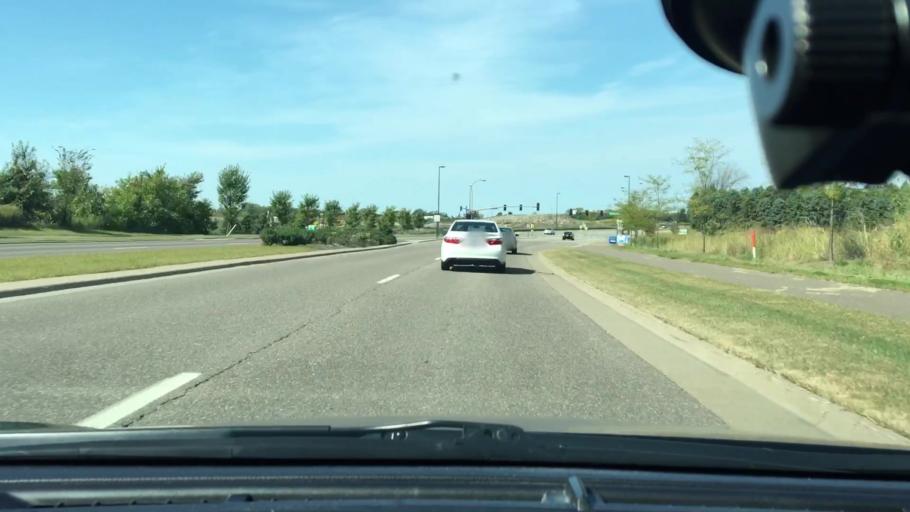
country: US
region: Minnesota
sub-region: Hennepin County
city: Corcoran
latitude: 45.0827
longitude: -93.5111
